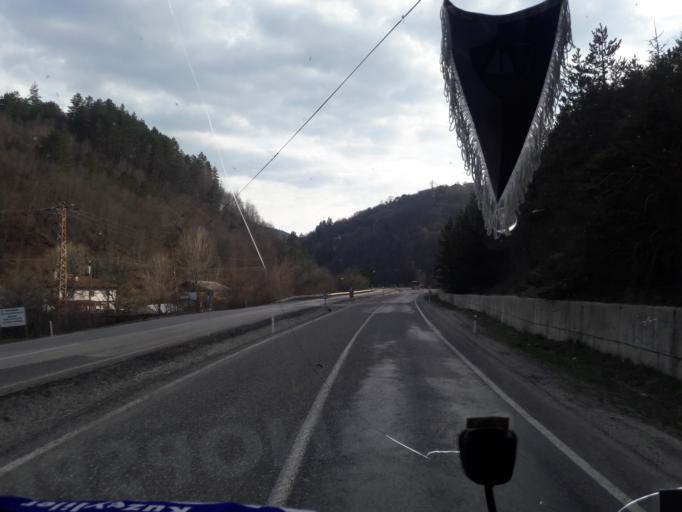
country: TR
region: Kastamonu
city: Kuzyaka
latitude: 41.1441
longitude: 33.7799
